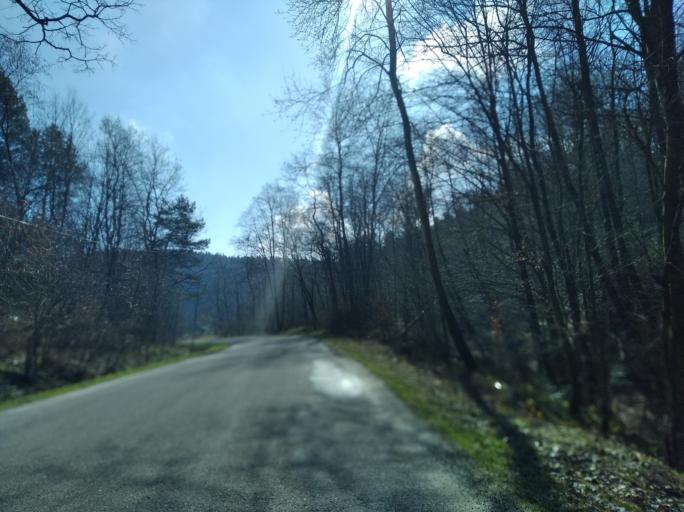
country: PL
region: Subcarpathian Voivodeship
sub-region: Powiat strzyzowski
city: Frysztak
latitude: 49.8695
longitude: 21.5583
